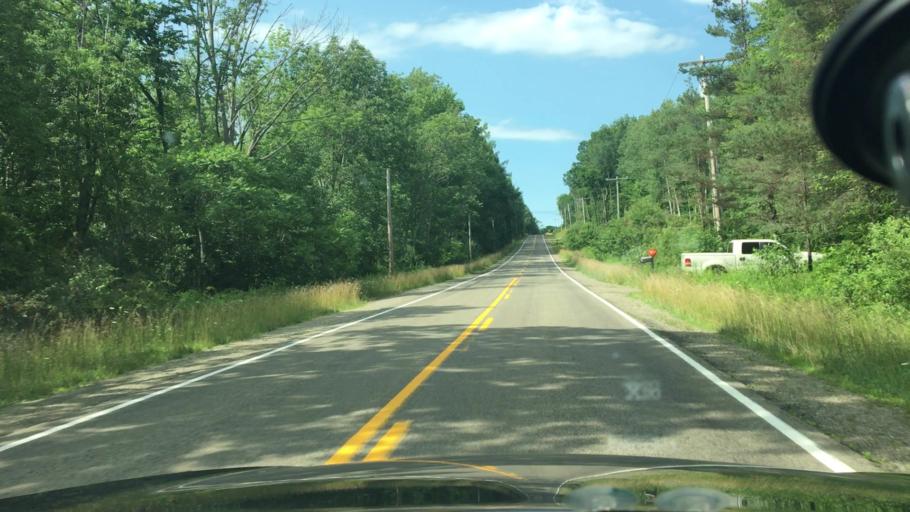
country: US
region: New York
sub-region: Chautauqua County
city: Lakewood
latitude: 42.2216
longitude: -79.3616
